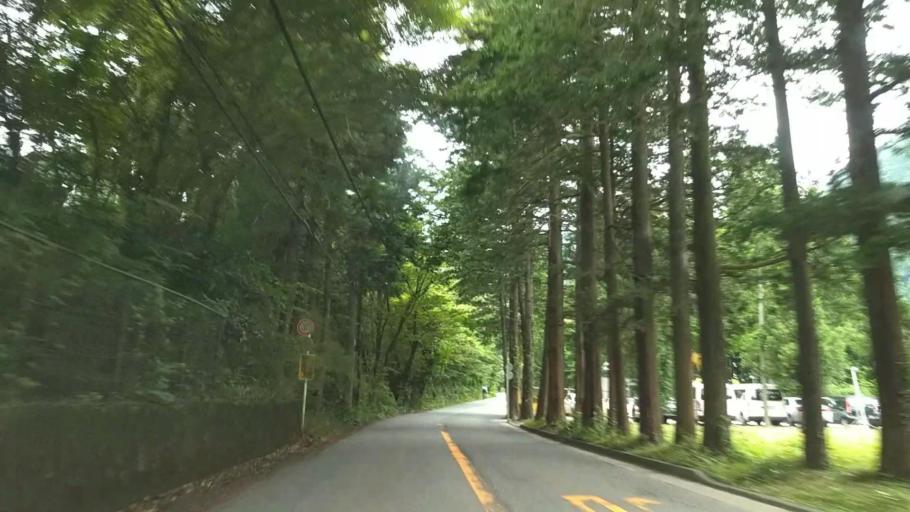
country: JP
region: Kanagawa
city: Hakone
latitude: 35.2221
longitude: 139.0815
